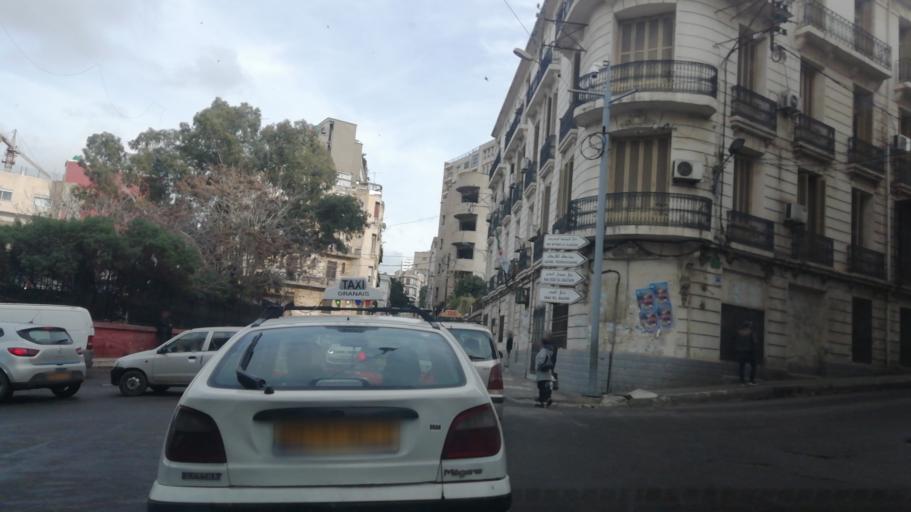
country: DZ
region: Oran
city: Oran
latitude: 35.7028
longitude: -0.6359
